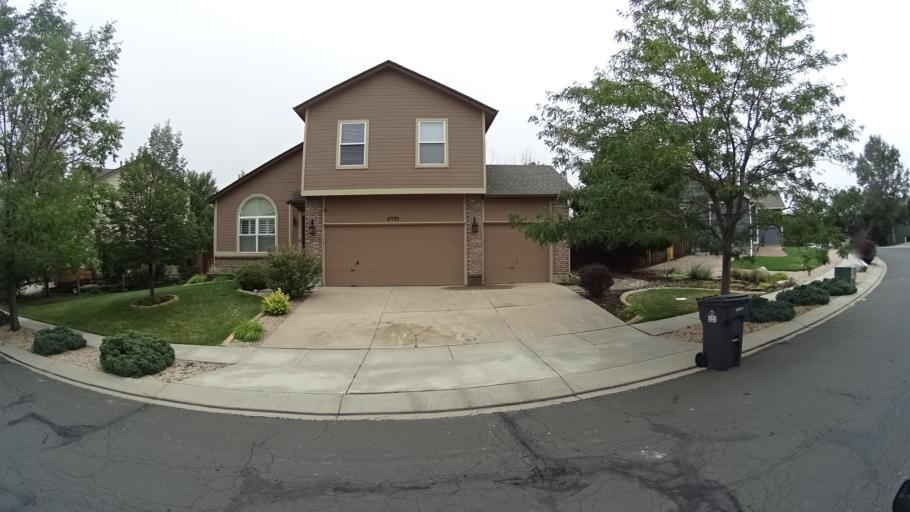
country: US
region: Colorado
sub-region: El Paso County
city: Black Forest
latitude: 38.9372
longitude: -104.7440
